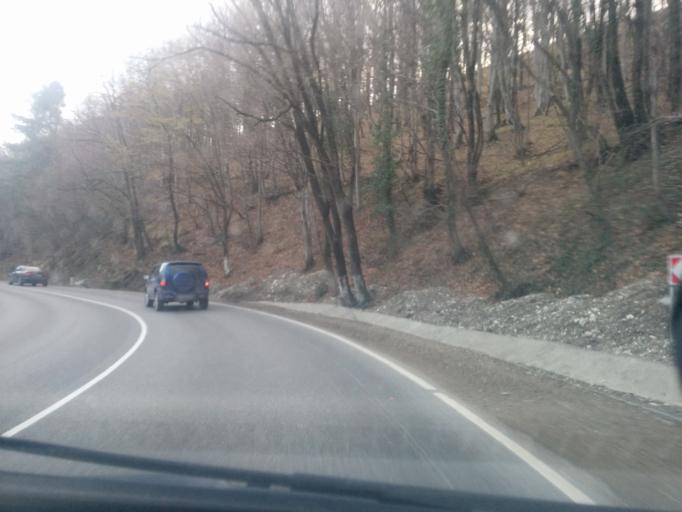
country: RU
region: Krasnodarskiy
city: Agoy
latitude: 44.1303
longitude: 39.0460
